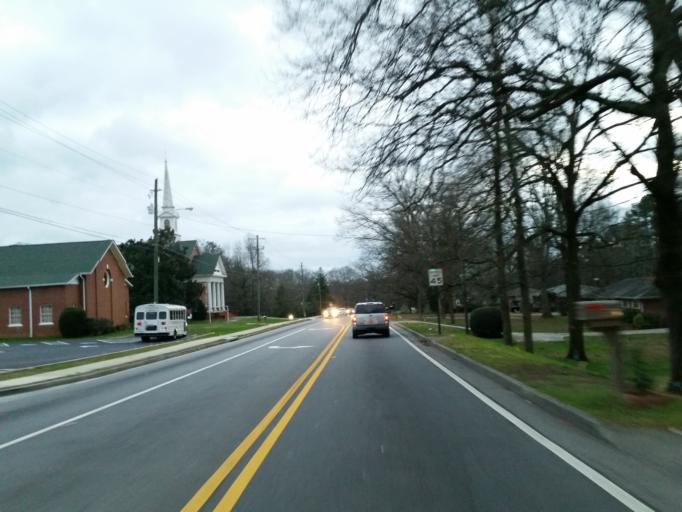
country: US
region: Georgia
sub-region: Cobb County
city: Mableton
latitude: 33.8644
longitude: -84.5772
